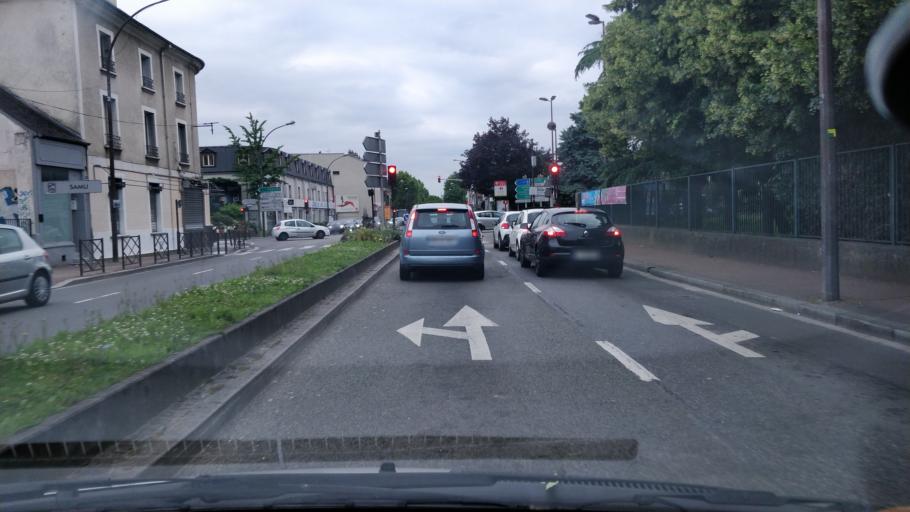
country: FR
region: Ile-de-France
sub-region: Departement de Seine-Saint-Denis
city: Livry-Gargan
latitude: 48.9168
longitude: 2.5322
